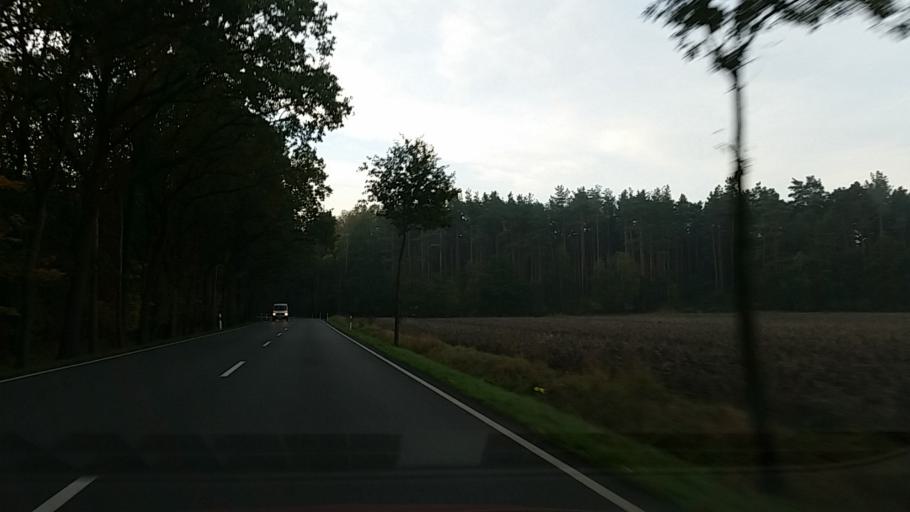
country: DE
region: Lower Saxony
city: Tulau
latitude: 52.6315
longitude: 10.8789
